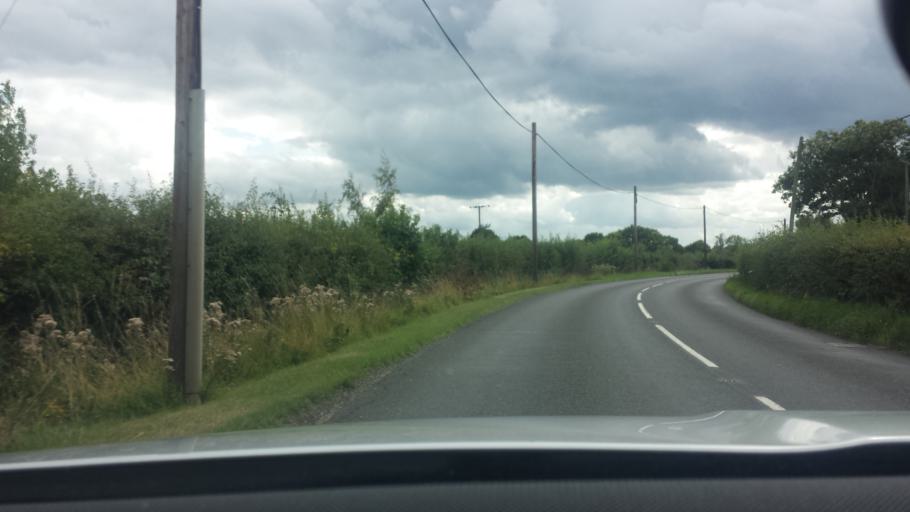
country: GB
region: England
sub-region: Kent
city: Marden
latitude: 51.1946
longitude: 0.5182
